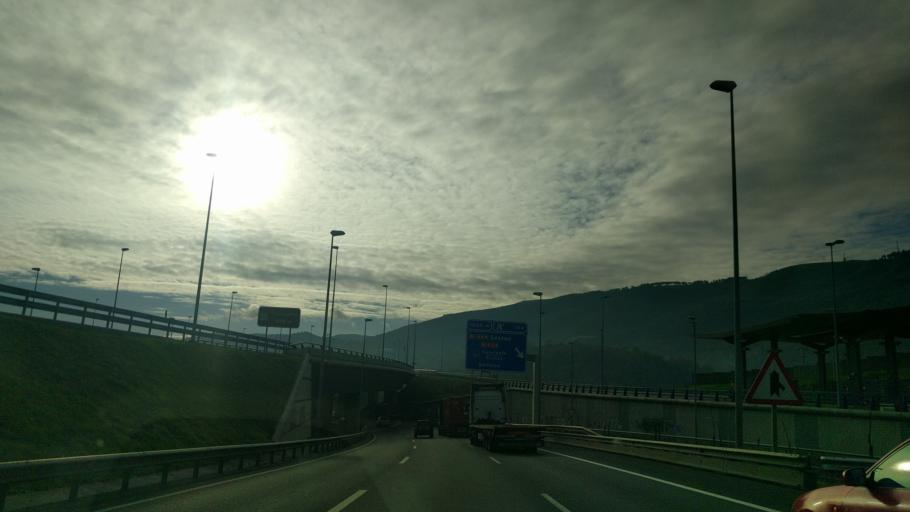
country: ES
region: Basque Country
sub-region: Bizkaia
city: Portugalete
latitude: 43.3031
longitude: -3.0242
